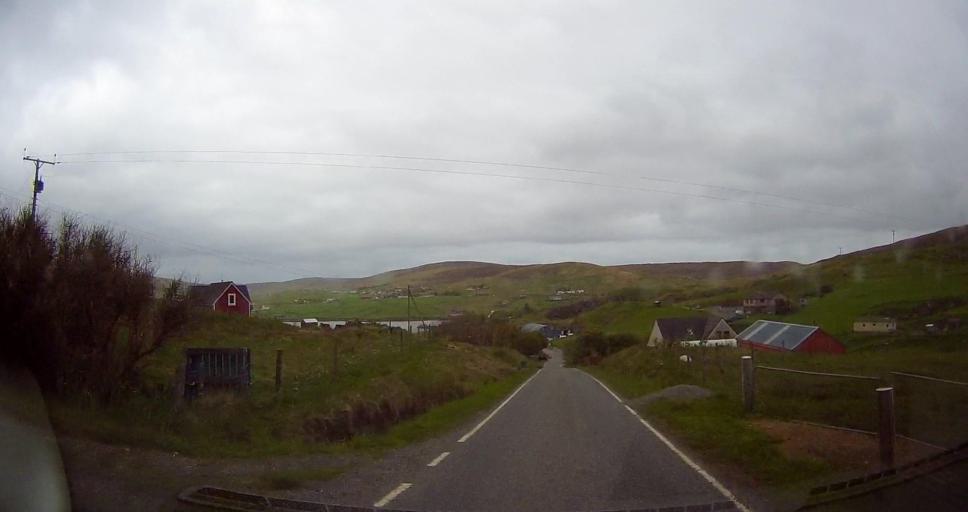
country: GB
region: Scotland
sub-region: Shetland Islands
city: Lerwick
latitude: 60.3444
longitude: -1.2745
